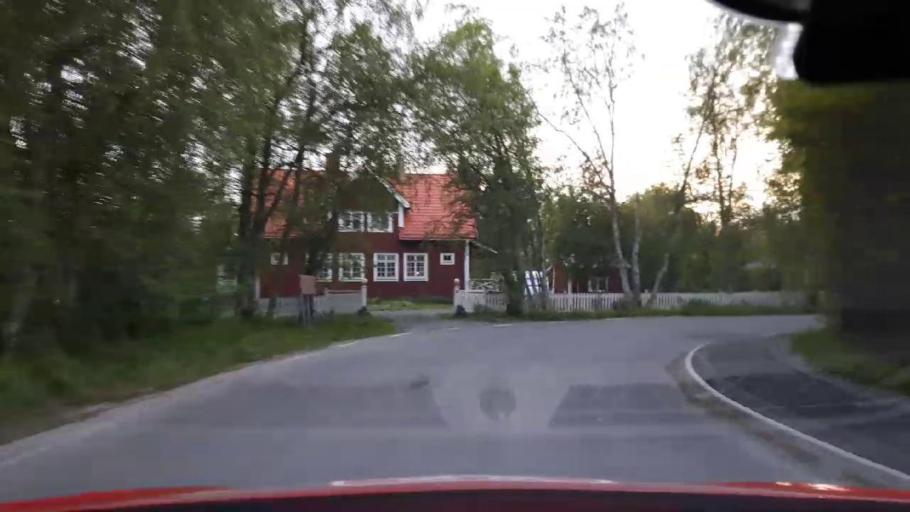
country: SE
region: Jaemtland
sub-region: OEstersunds Kommun
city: Ostersund
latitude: 62.9932
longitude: 14.5754
